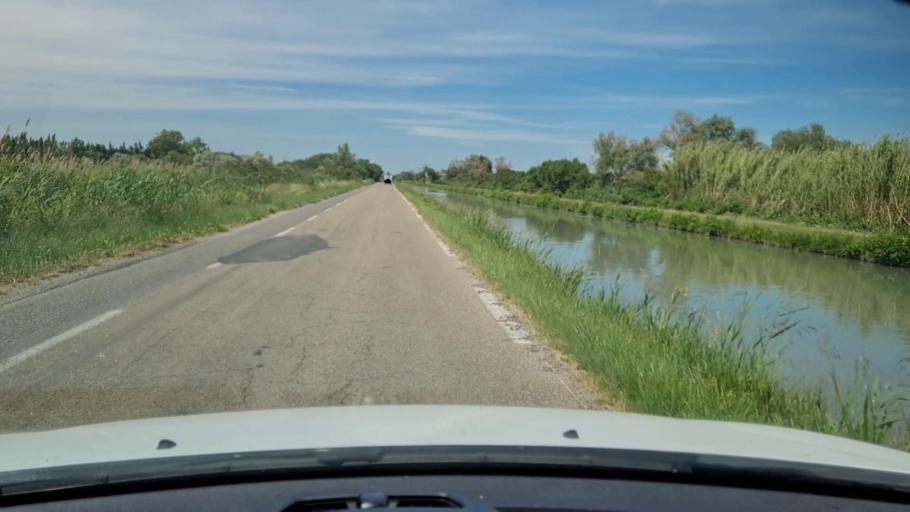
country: FR
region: Languedoc-Roussillon
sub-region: Departement du Gard
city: Vauvert
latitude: 43.5969
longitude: 4.3409
